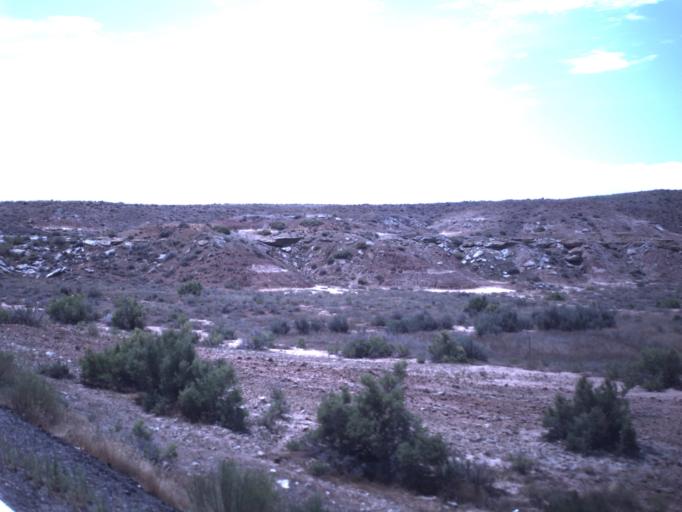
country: US
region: Utah
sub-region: Uintah County
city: Maeser
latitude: 40.3146
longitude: -109.6923
